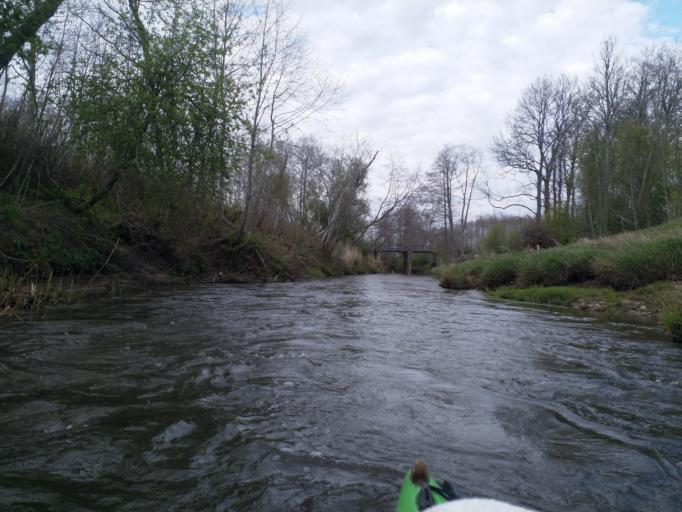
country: LV
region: Alsunga
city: Alsunga
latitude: 57.1249
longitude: 21.5496
